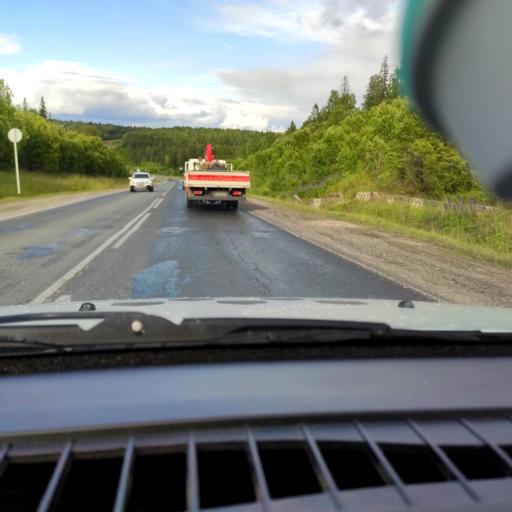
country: RU
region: Perm
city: Sylva
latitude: 58.2986
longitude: 56.7658
